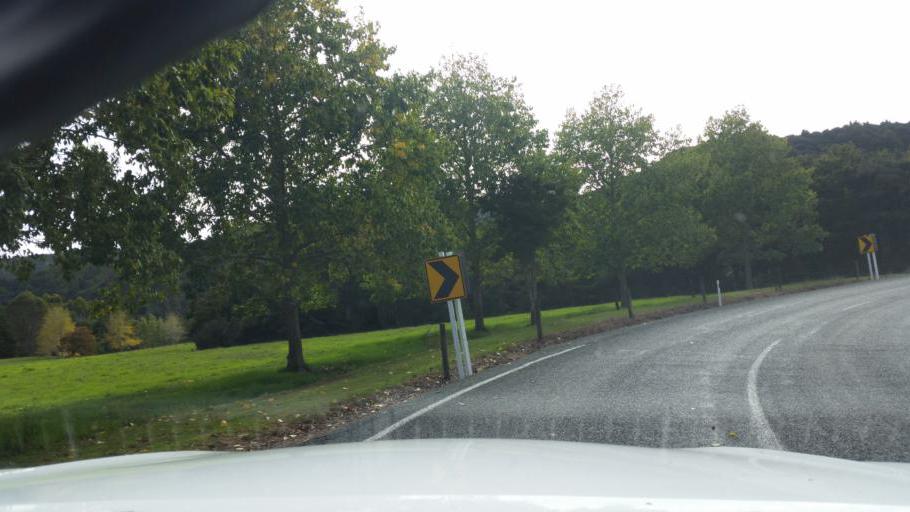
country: NZ
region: Northland
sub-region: Whangarei
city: Ruakaka
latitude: -36.0841
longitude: 174.5351
